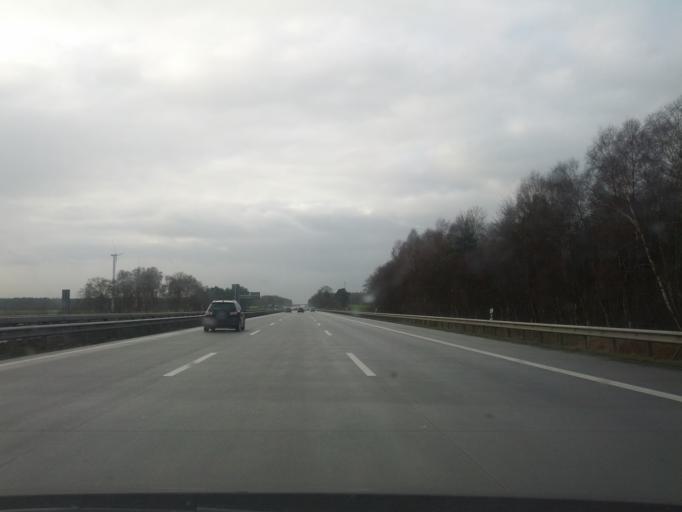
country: DE
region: Lower Saxony
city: Ottersberg
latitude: 53.0773
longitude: 9.1471
